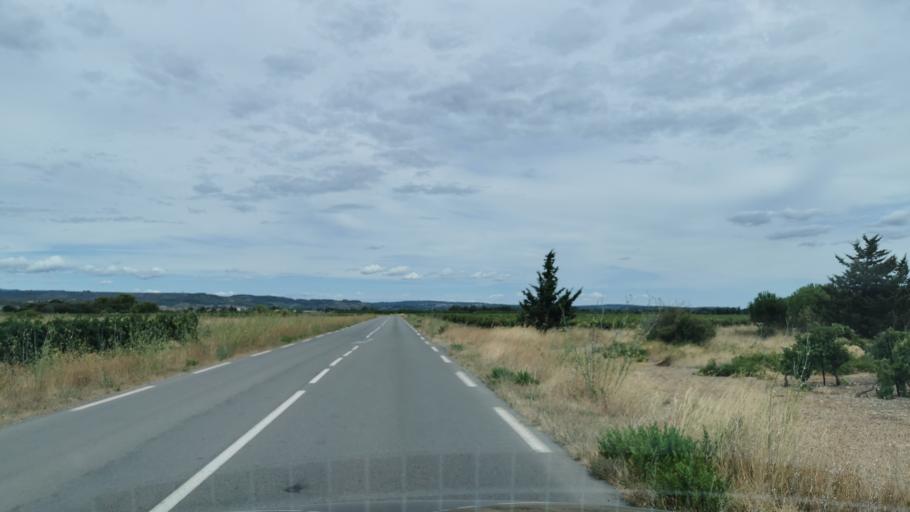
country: FR
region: Languedoc-Roussillon
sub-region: Departement de l'Aude
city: Argeliers
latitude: 43.2920
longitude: 2.9021
